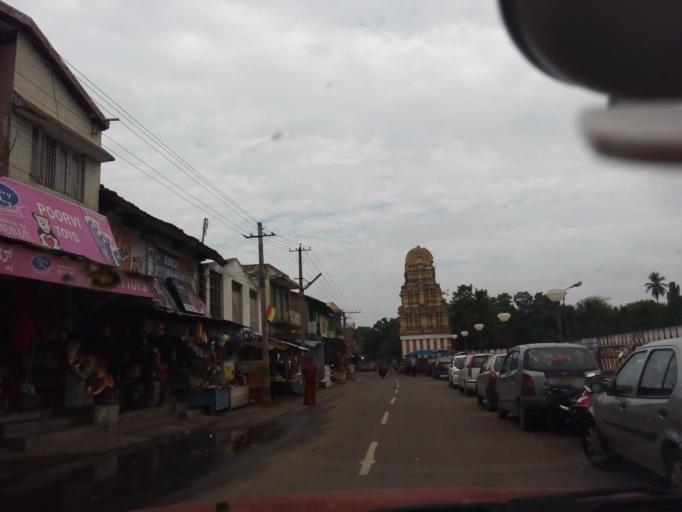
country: IN
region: Karnataka
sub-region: Hassan
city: Shravanabelagola
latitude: 12.8574
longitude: 76.4870
